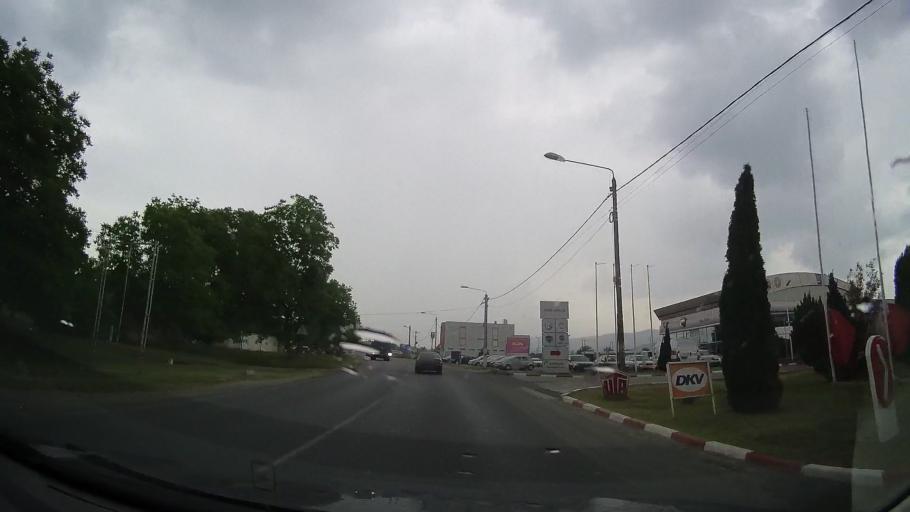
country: RO
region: Caras-Severin
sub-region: Municipiul Caransebes
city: Caransebes
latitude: 45.3891
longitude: 22.2284
